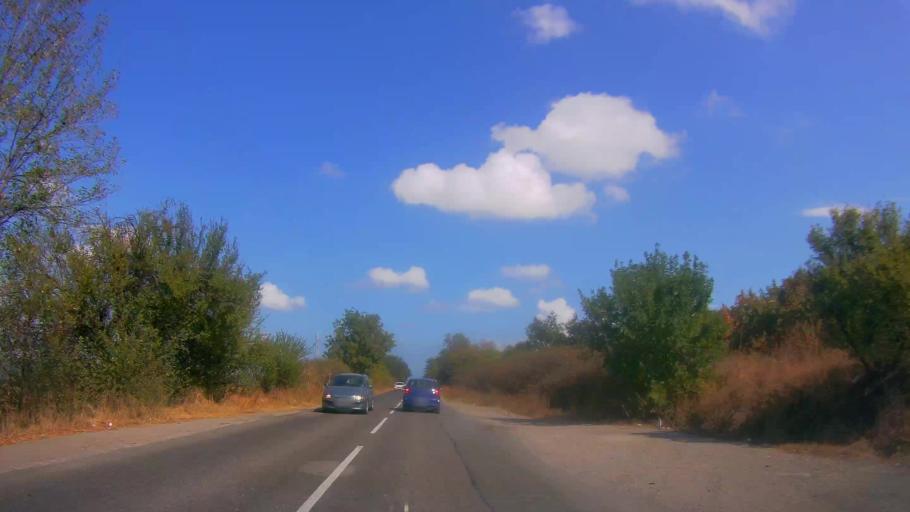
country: BG
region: Burgas
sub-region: Obshtina Burgas
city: Burgas
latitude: 42.4774
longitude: 27.4093
